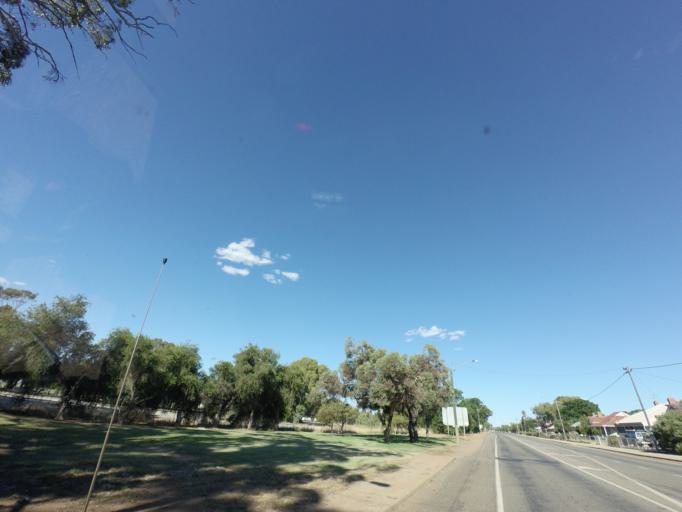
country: AU
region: Western Australia
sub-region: Merredin
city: Merredin
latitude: -31.4829
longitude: 118.2730
